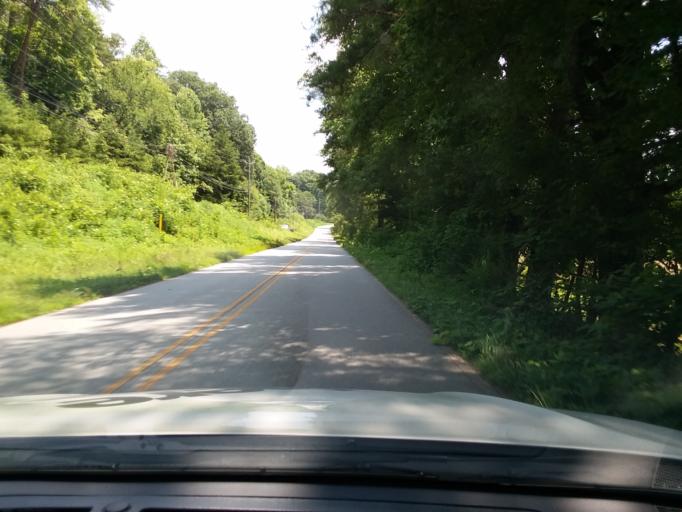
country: US
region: Georgia
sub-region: Rabun County
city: Clayton
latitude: 34.8018
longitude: -83.4277
